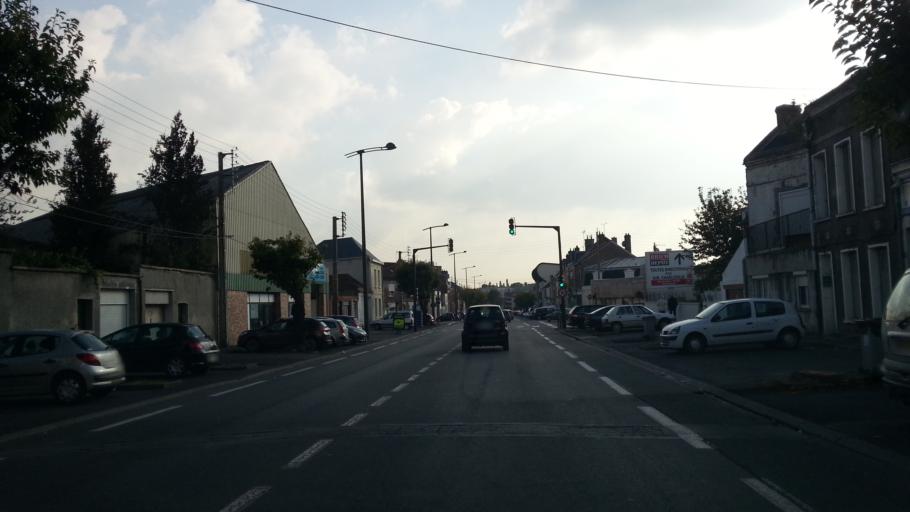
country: FR
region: Picardie
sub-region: Departement de l'Aisne
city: Saint-Quentin
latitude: 49.8464
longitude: 3.2794
